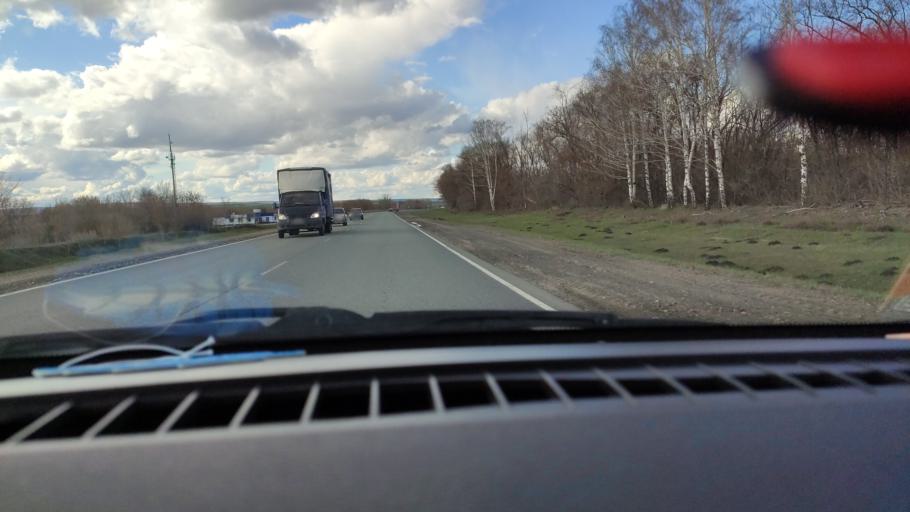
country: RU
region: Saratov
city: Tersa
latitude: 52.0913
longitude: 47.5449
